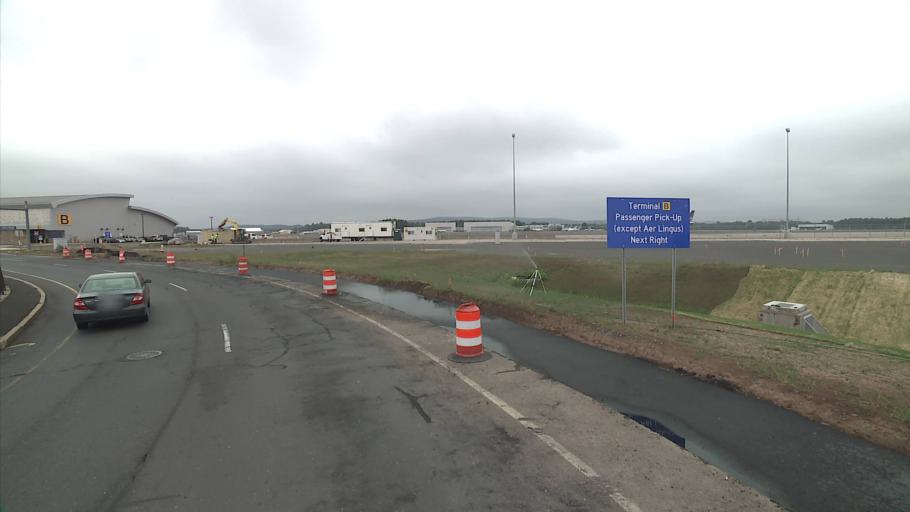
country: US
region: Connecticut
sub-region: Hartford County
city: Windsor Locks
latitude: 41.9333
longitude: -72.6879
